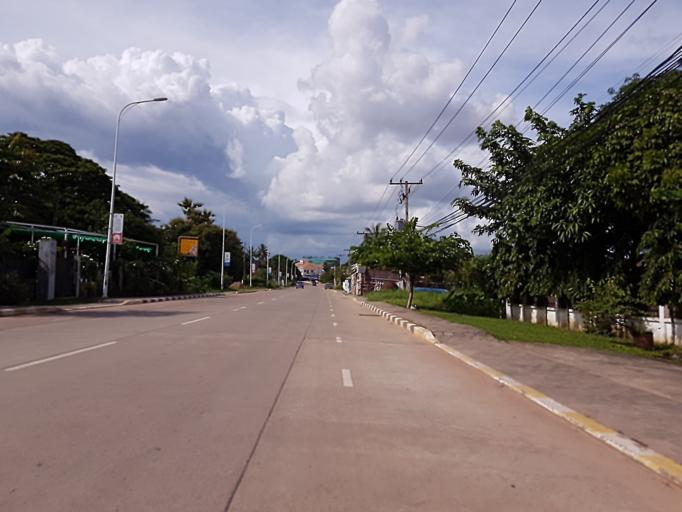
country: LA
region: Vientiane
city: Vientiane
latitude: 17.9281
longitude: 102.6252
